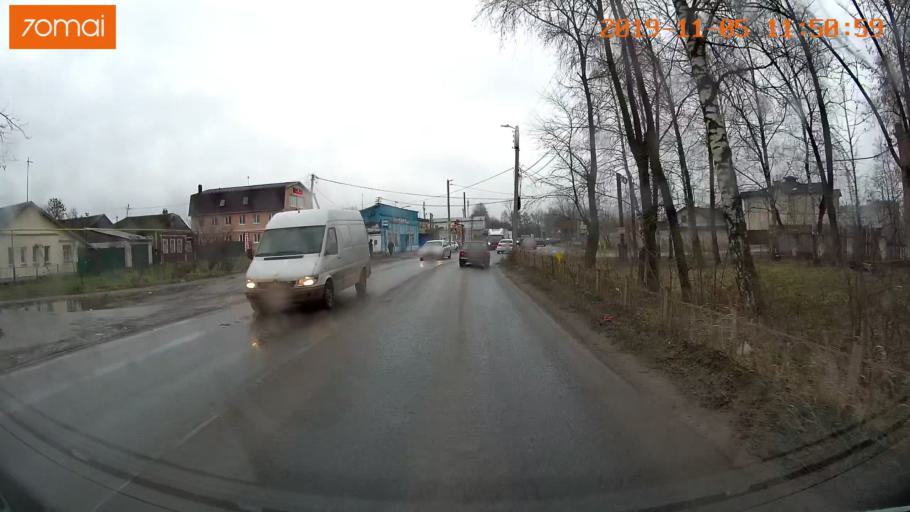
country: RU
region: Ivanovo
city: Bogorodskoye
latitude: 57.0070
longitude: 41.0240
